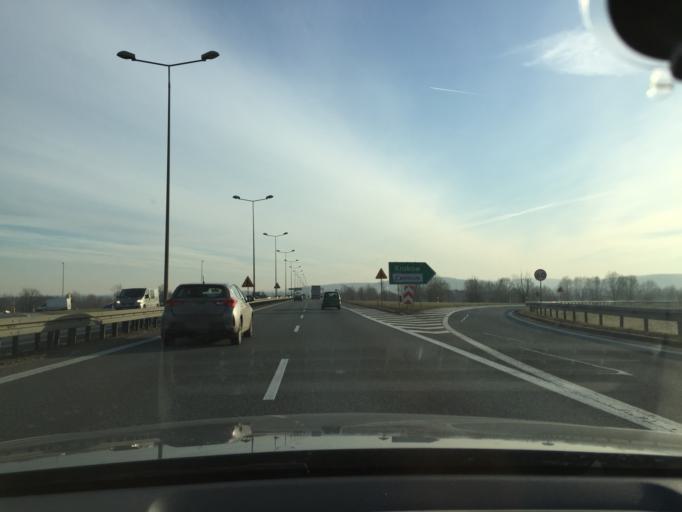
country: PL
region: Lesser Poland Voivodeship
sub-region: Powiat krakowski
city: Kryspinow
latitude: 50.0362
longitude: 19.8135
